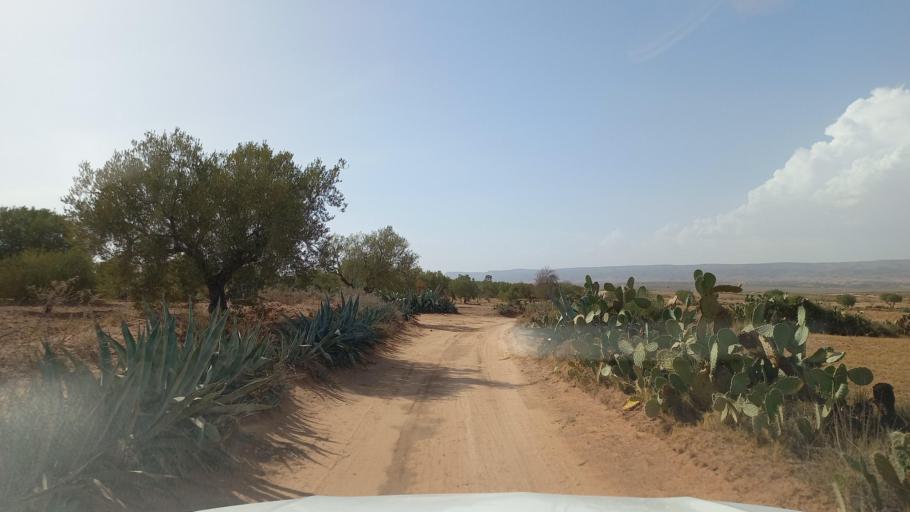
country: TN
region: Al Qasrayn
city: Kasserine
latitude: 35.2110
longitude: 8.9794
